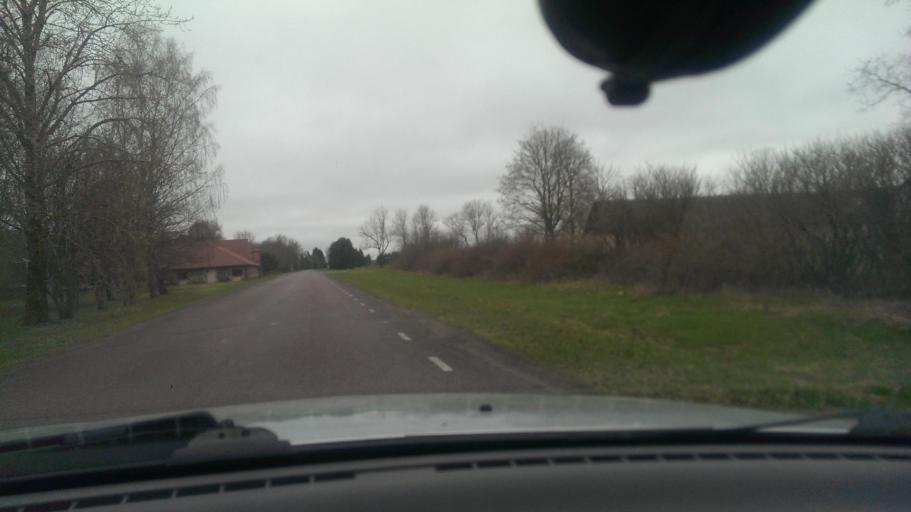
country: EE
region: Tartu
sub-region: Tartu linn
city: Tartu
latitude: 58.3574
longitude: 26.8827
